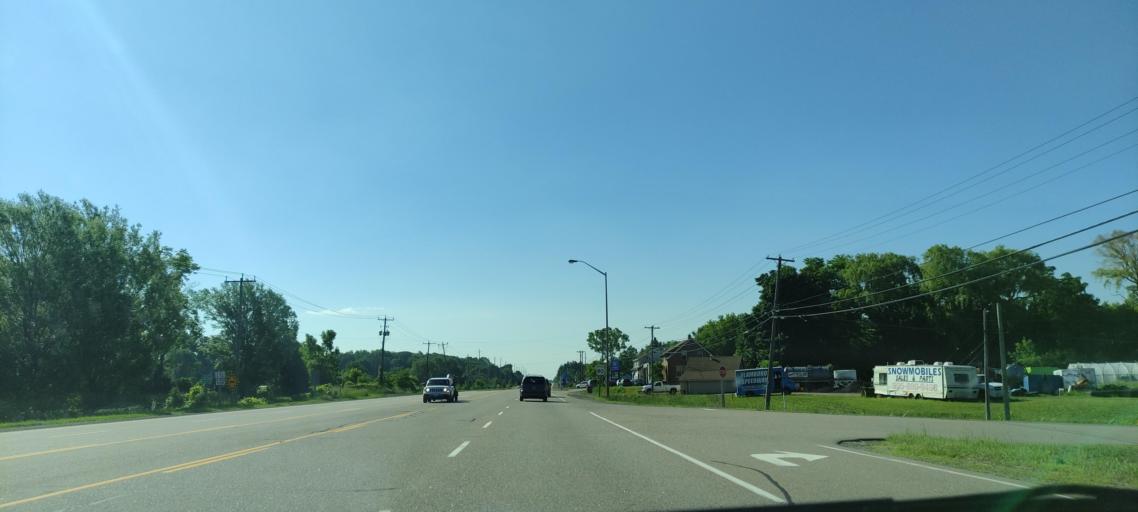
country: CA
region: Ontario
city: Ancaster
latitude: 43.3377
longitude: -79.9528
